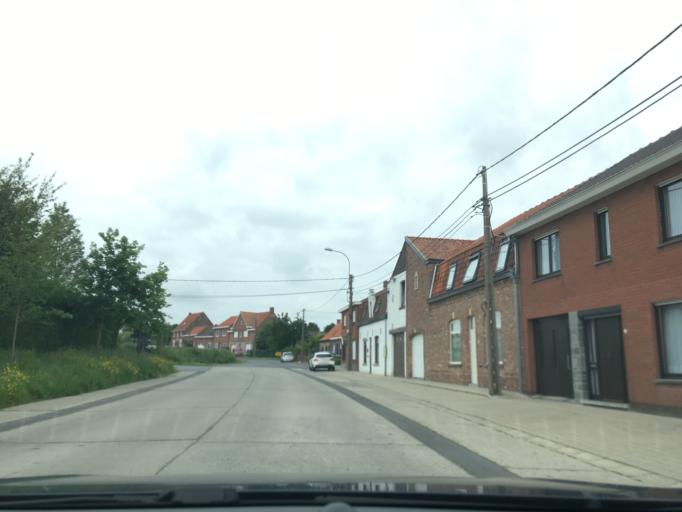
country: BE
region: Flanders
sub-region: Provincie West-Vlaanderen
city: Moorslede
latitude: 50.8479
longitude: 3.0765
